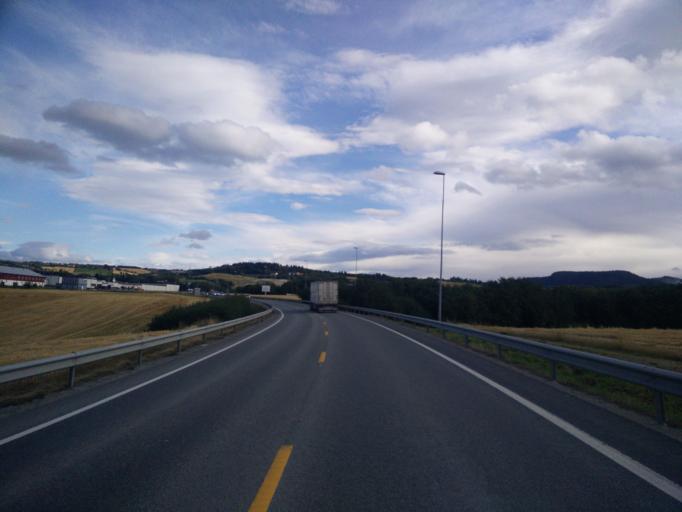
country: NO
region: Sor-Trondelag
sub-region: Melhus
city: Melhus
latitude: 63.3222
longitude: 10.3146
